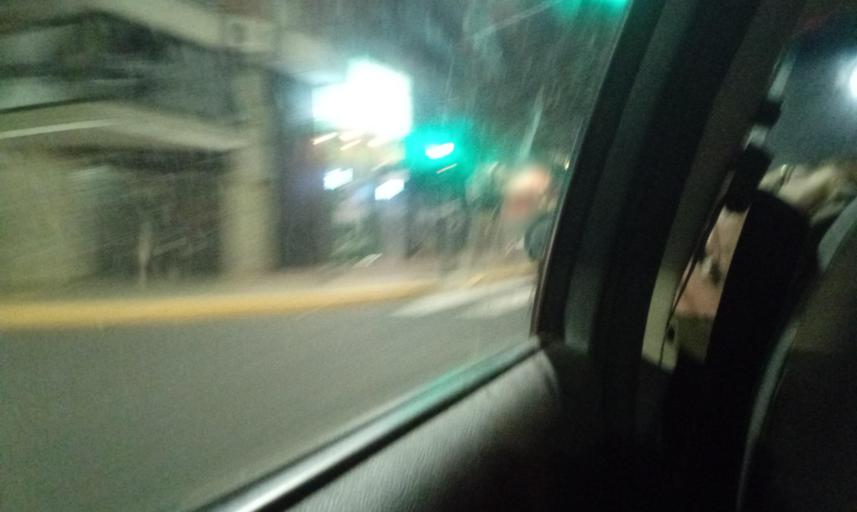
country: AR
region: Buenos Aires F.D.
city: Villa Santa Rita
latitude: -34.6283
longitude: -58.4789
